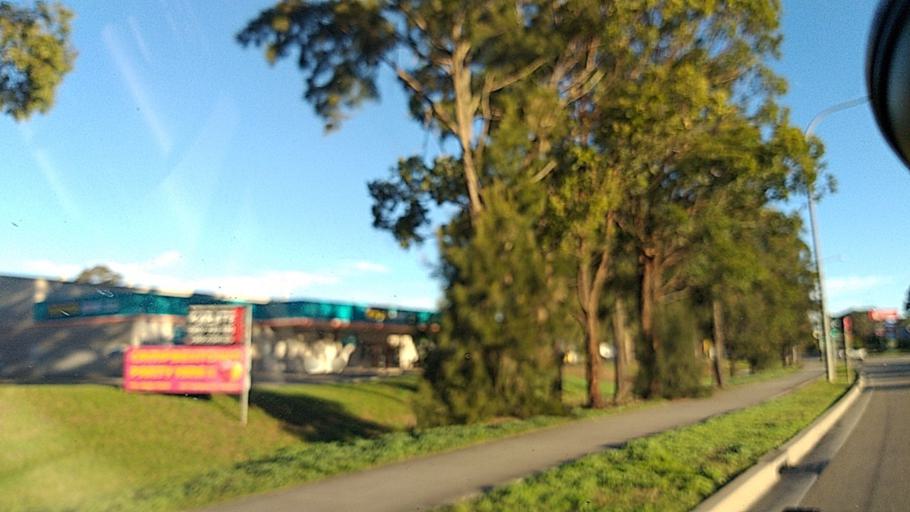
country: AU
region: New South Wales
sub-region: Campbelltown Municipality
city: Leumeah
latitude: -34.0516
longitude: 150.8250
